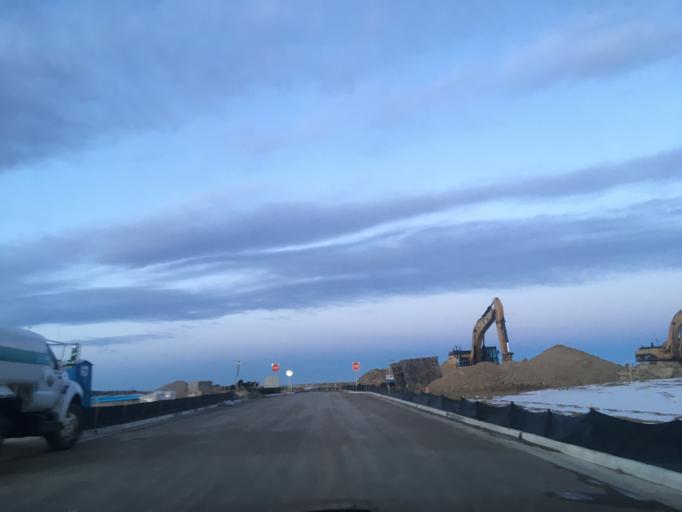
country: US
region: Colorado
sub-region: Boulder County
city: Superior
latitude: 39.9492
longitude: -105.1578
